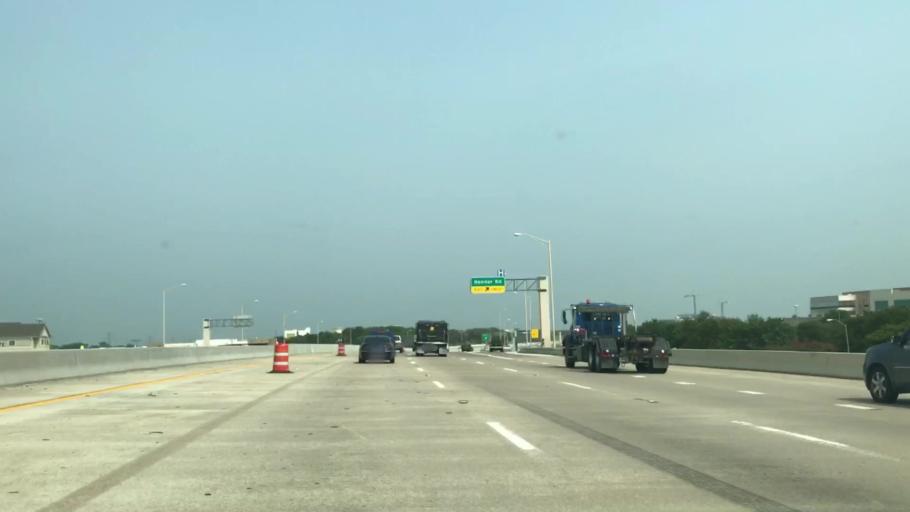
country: US
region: Texas
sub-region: Collin County
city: Plano
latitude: 33.0025
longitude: -96.6822
